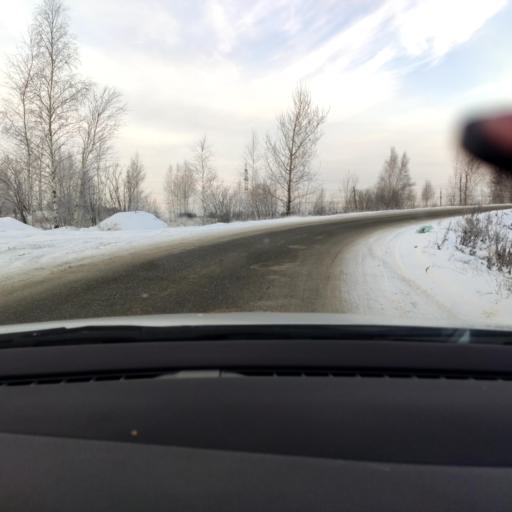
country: RU
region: Tatarstan
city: Vysokaya Gora
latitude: 55.8711
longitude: 49.2936
